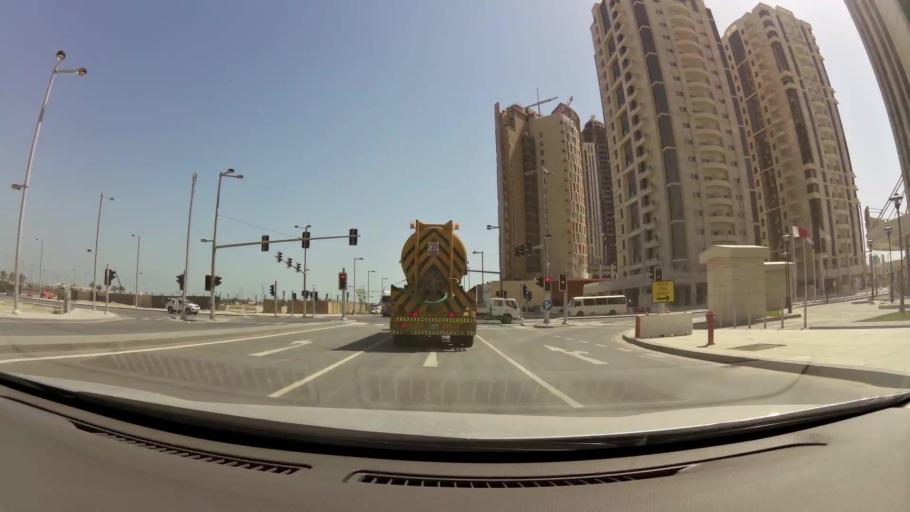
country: QA
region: Baladiyat ad Dawhah
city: Doha
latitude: 25.3865
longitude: 51.5240
